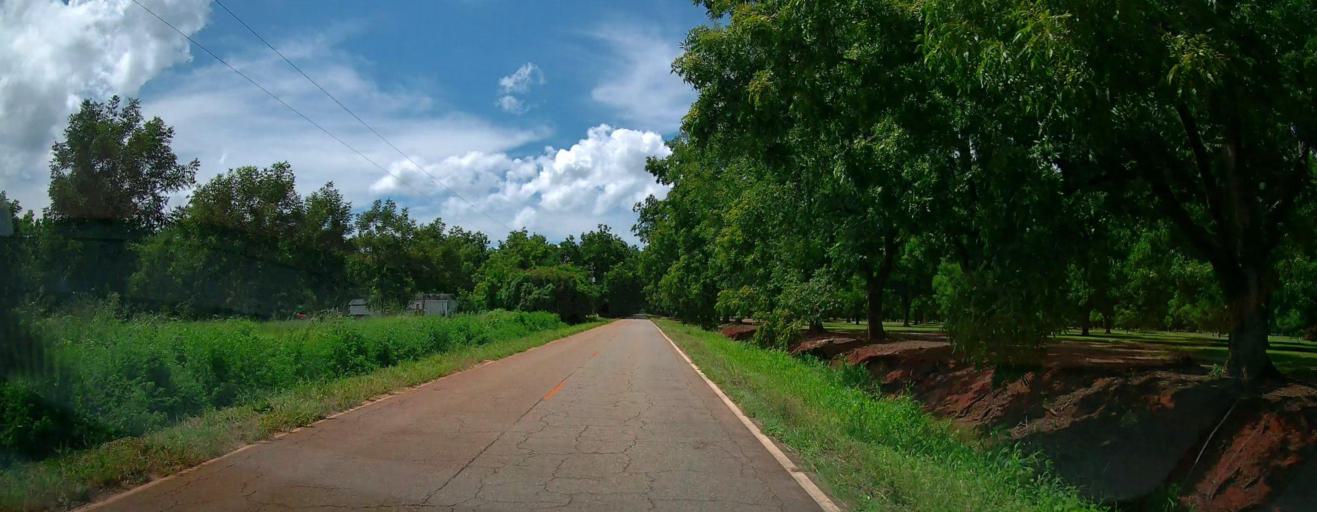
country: US
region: Georgia
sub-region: Houston County
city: Perry
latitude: 32.5212
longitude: -83.7854
